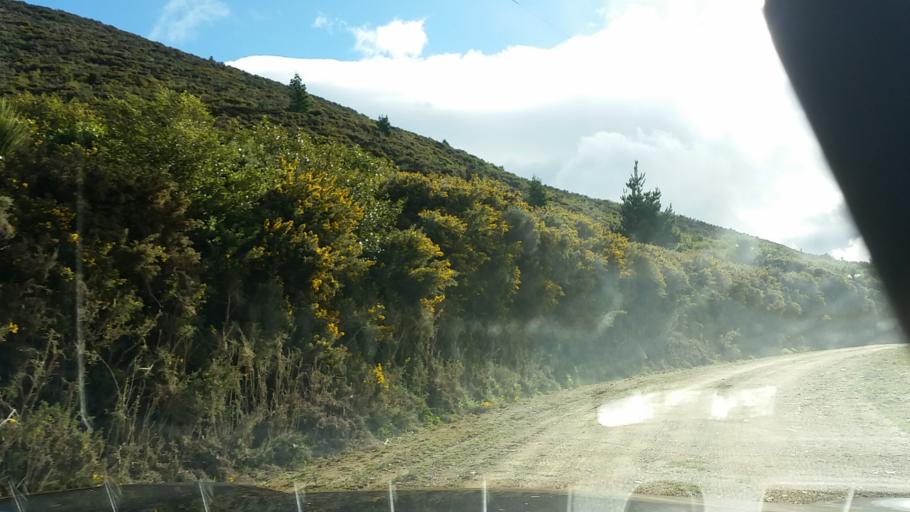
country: NZ
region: Marlborough
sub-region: Marlborough District
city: Picton
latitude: -40.9719
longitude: 173.8932
